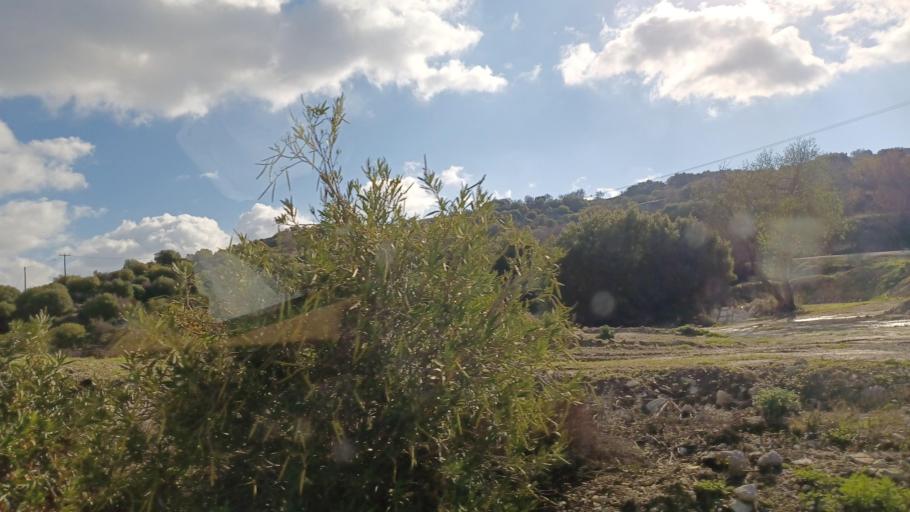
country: CY
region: Limassol
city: Pachna
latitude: 34.8328
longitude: 32.6851
